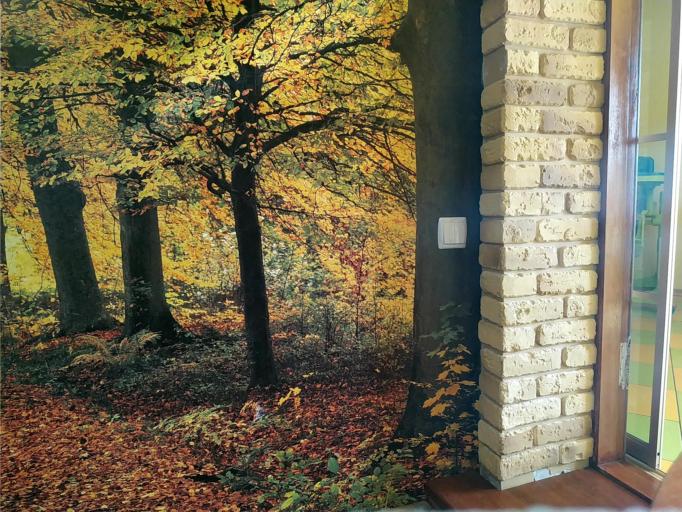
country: RU
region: Smolensk
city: Katyn'
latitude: 55.0023
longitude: 31.7631
